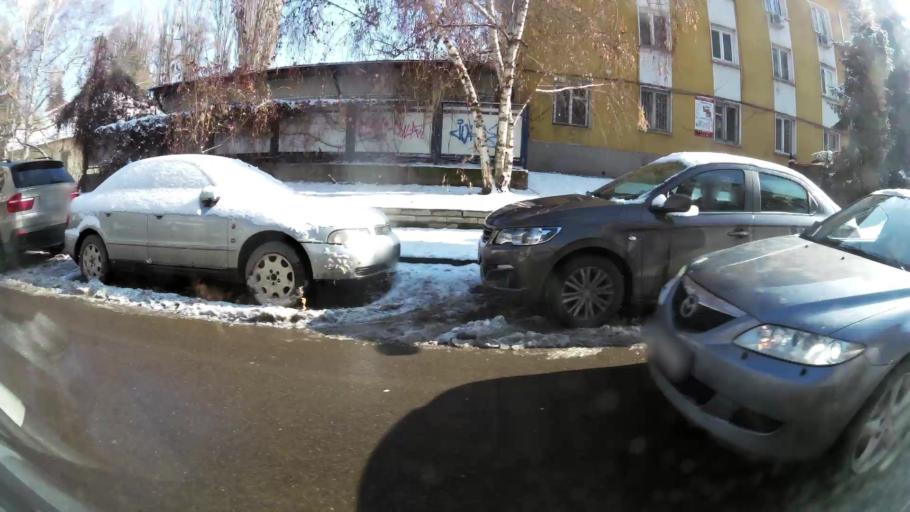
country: BG
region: Sofia-Capital
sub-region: Stolichna Obshtina
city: Sofia
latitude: 42.6765
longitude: 23.3115
